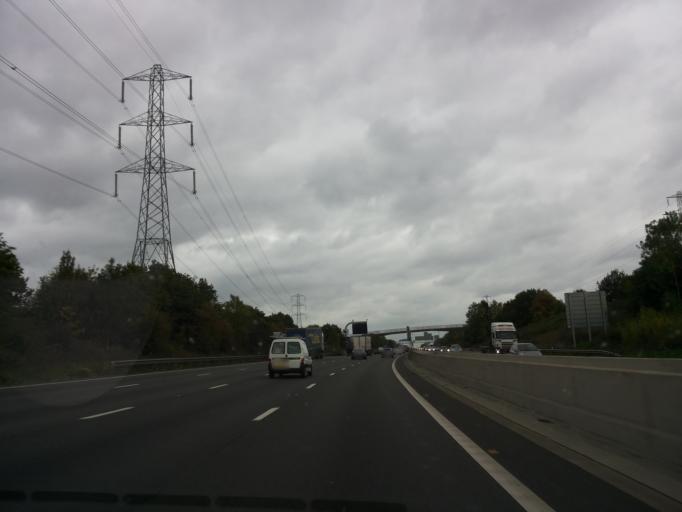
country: GB
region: England
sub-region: Hertfordshire
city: Potters Bar
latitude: 51.6862
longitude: -0.1985
